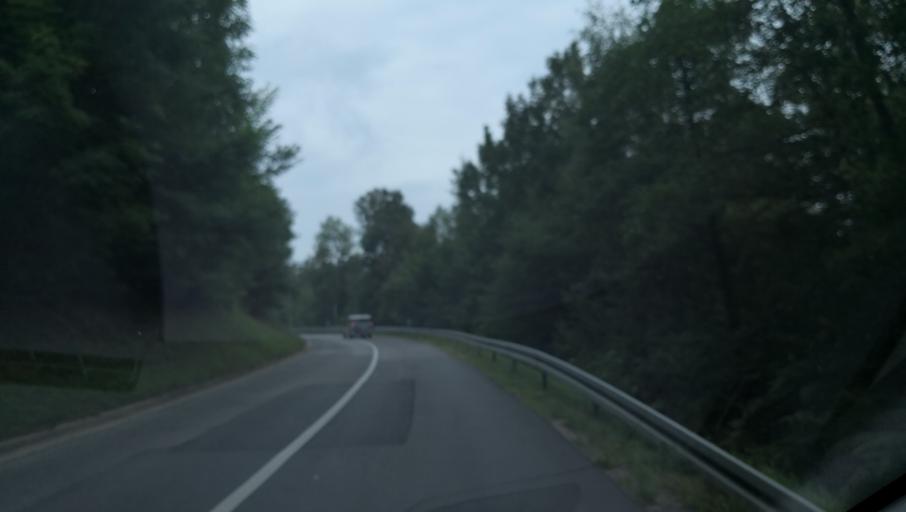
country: HR
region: Karlovacka
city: Ozalj
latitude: 45.5213
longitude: 15.3937
